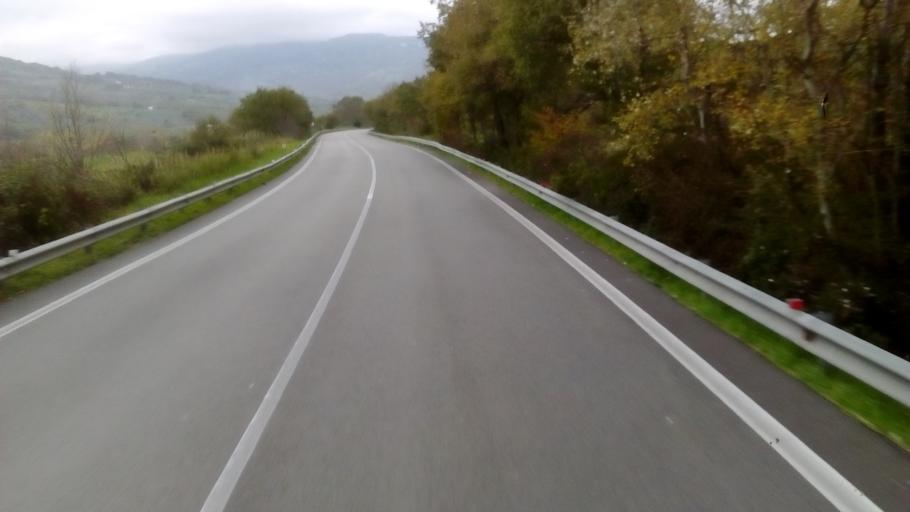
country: IT
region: Abruzzo
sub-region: Provincia di Chieti
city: Celenza sul Trigno
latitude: 41.8834
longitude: 14.6064
